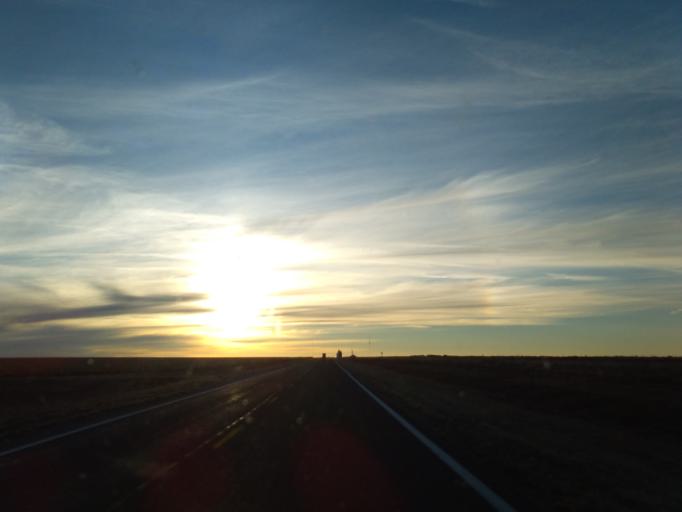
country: US
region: Kansas
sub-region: Logan County
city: Oakley
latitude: 39.0716
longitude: -101.2108
